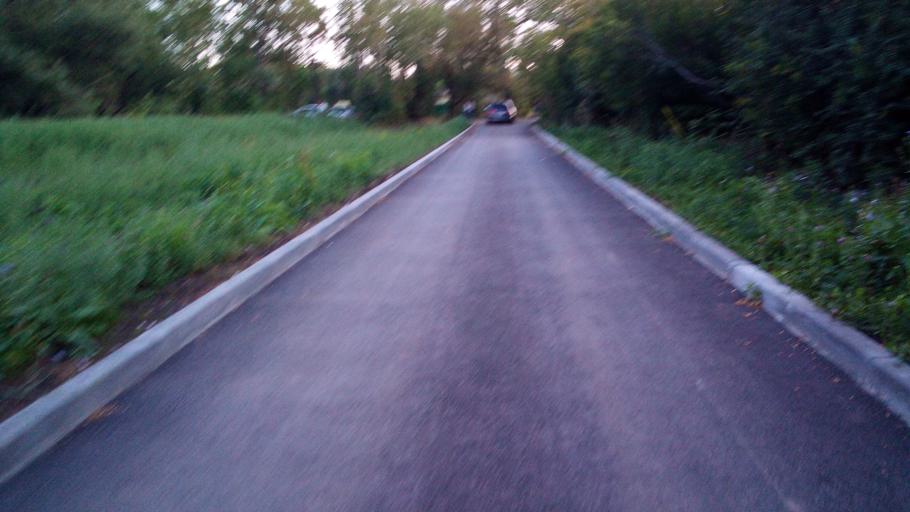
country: RU
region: Chelyabinsk
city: Potanino
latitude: 55.2915
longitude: 61.5115
